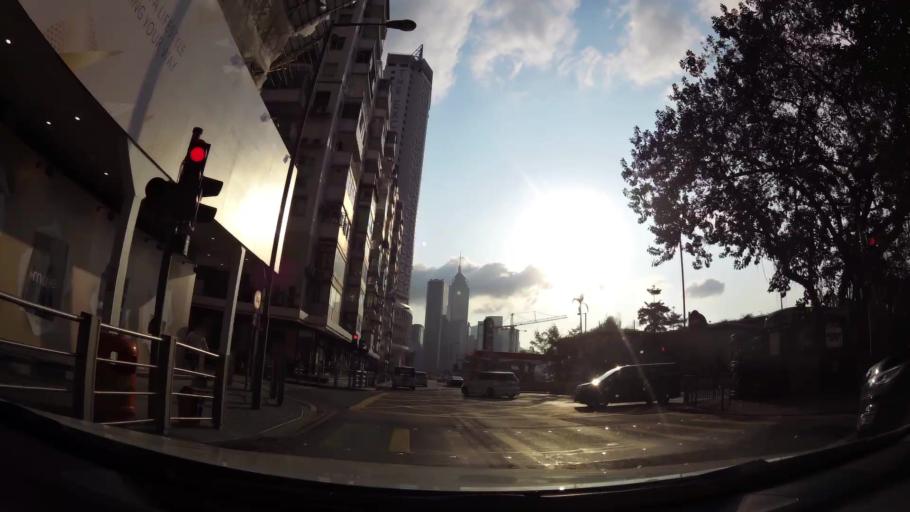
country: HK
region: Wanchai
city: Wan Chai
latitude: 22.2829
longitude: 114.1858
